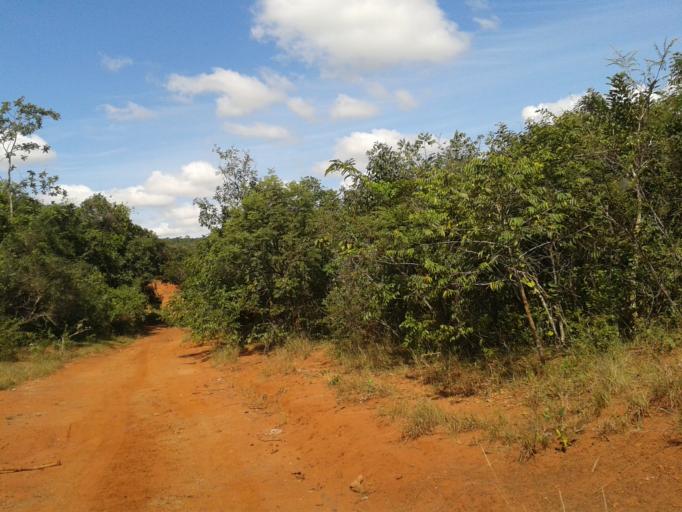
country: BR
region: Minas Gerais
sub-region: Campina Verde
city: Campina Verde
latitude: -19.4394
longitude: -49.7039
